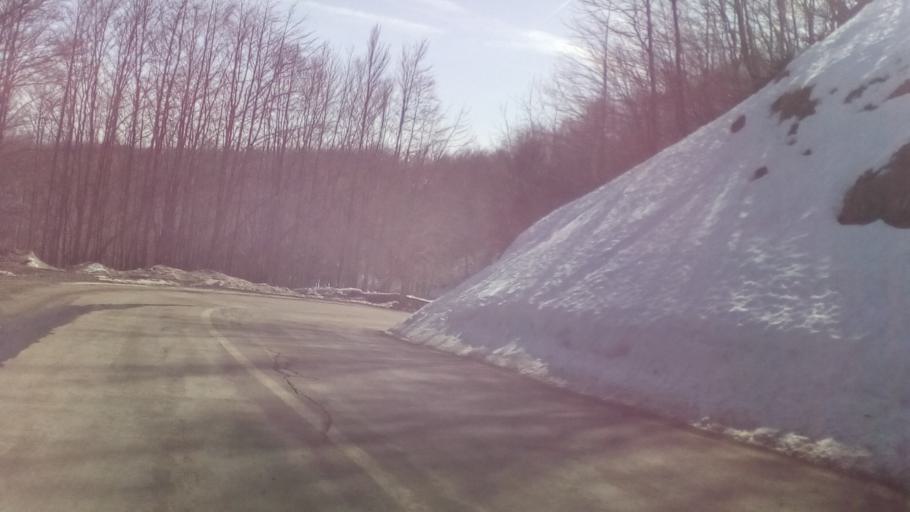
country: IT
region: Tuscany
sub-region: Provincia di Lucca
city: Castiglione di Garfagnana
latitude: 44.2063
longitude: 10.4901
